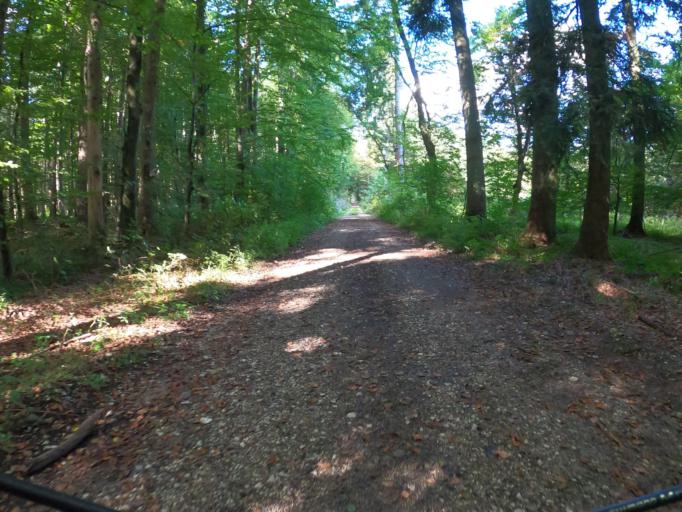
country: DE
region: Bavaria
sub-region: Swabia
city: Roggenburg
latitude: 48.3215
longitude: 10.2447
